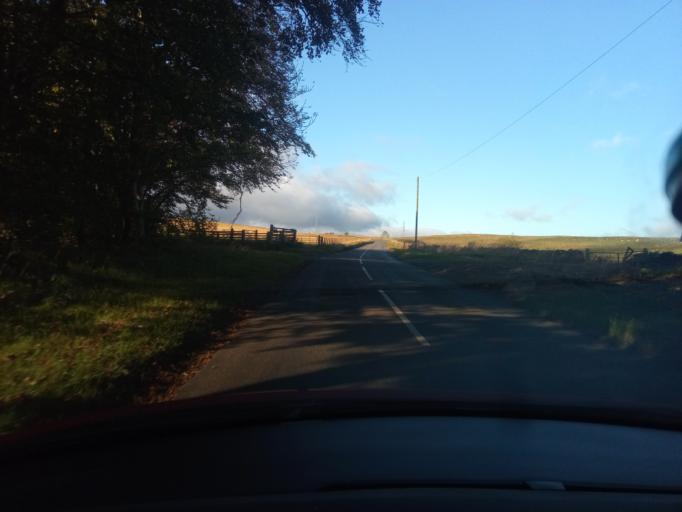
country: GB
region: Scotland
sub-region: The Scottish Borders
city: Lauder
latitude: 55.7184
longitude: -2.7682
